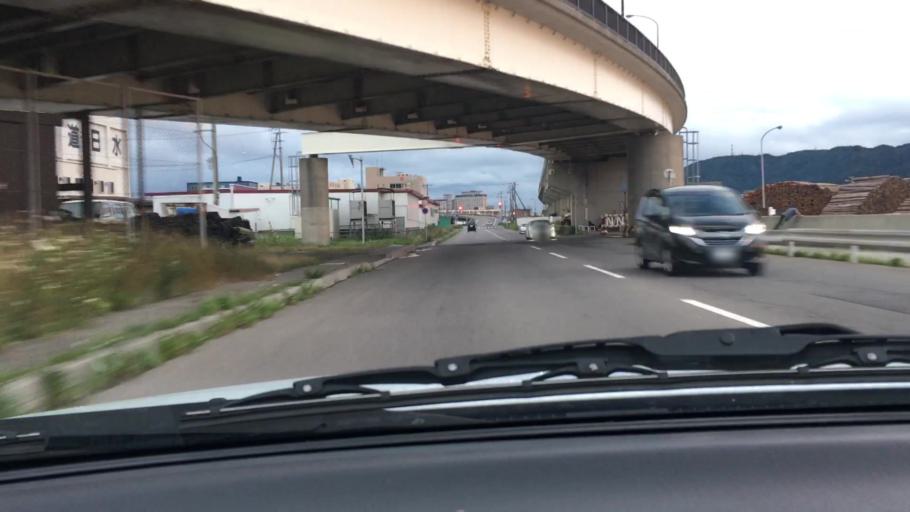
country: JP
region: Hokkaido
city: Hakodate
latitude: 41.7852
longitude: 140.7271
